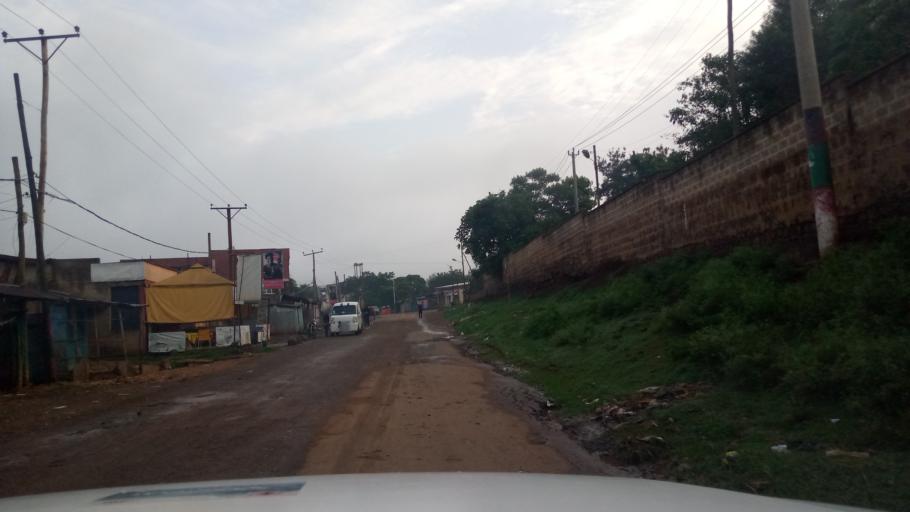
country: ET
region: Oromiya
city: Jima
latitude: 7.6824
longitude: 36.8499
